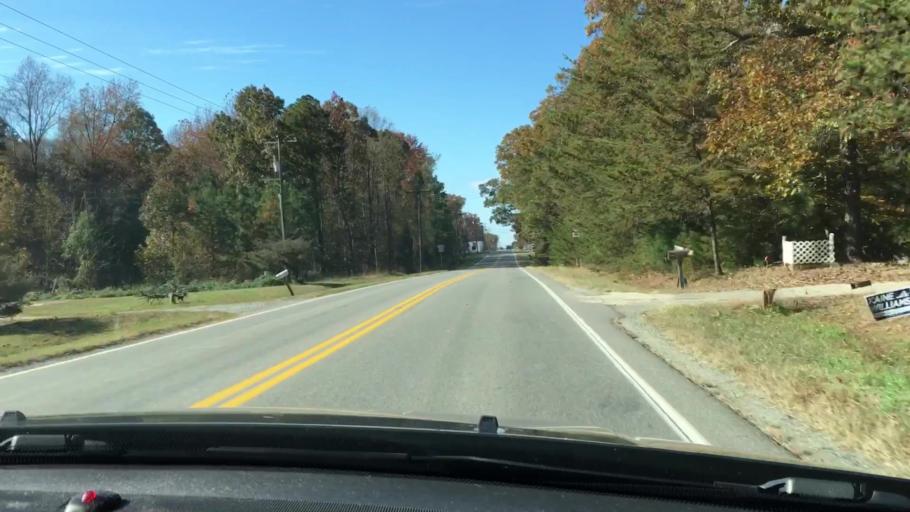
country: US
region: Virginia
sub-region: King William County
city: King William
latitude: 37.7162
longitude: -77.0696
